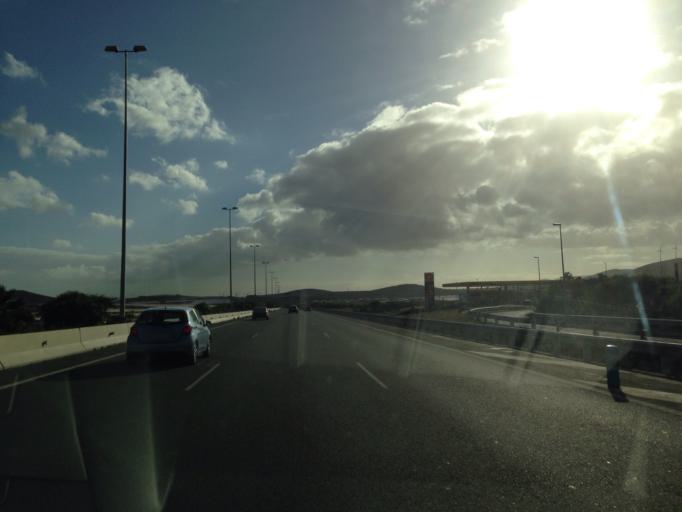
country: ES
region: Canary Islands
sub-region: Provincia de Las Palmas
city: Cruce de Arinaga
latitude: 27.9003
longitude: -15.4037
